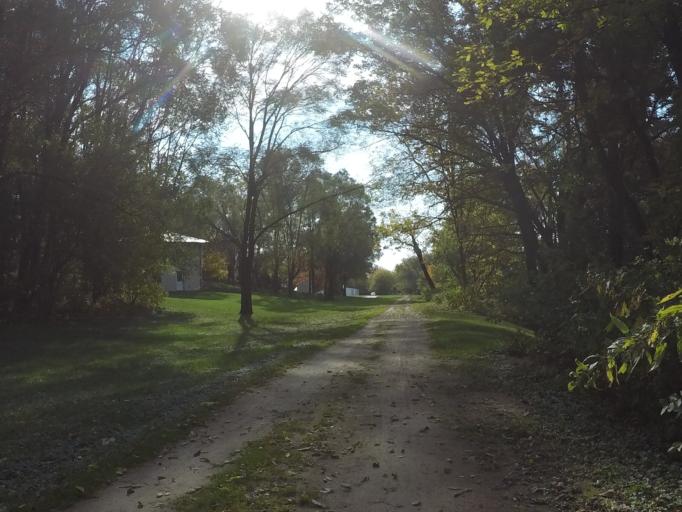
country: US
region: Wisconsin
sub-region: Iowa County
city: Barneveld
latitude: 43.0204
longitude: -89.8327
